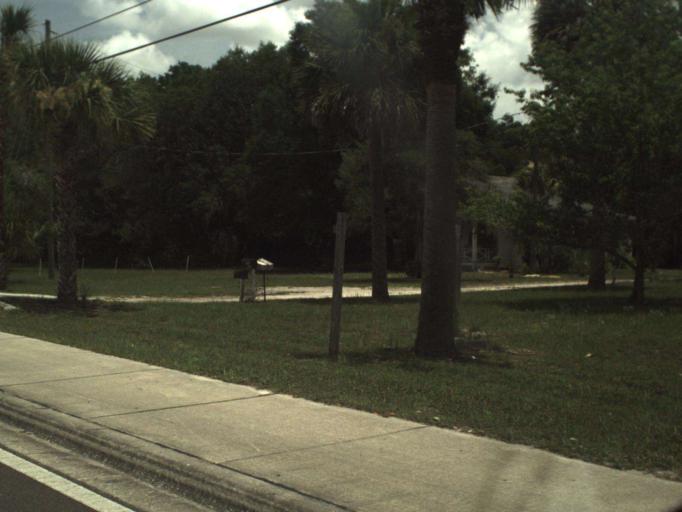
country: US
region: Florida
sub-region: Seminole County
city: Oviedo
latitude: 28.6475
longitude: -81.2305
